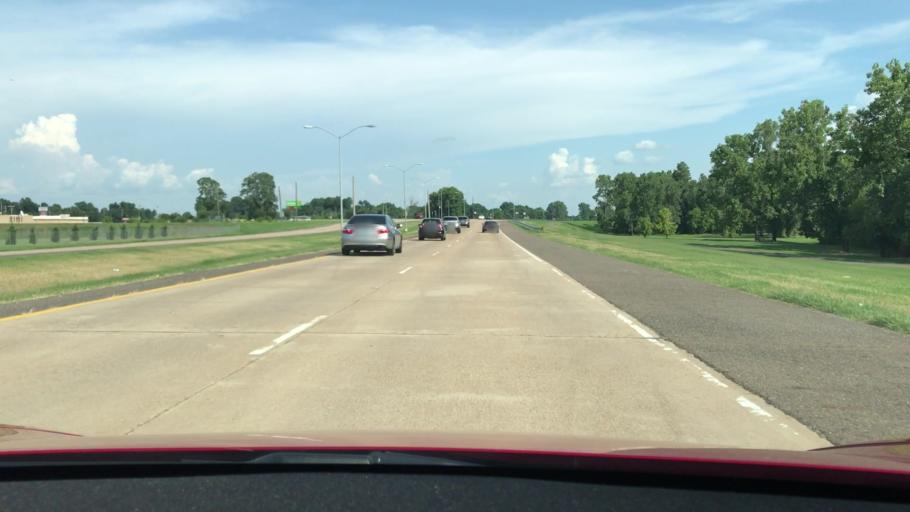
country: US
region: Louisiana
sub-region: Bossier Parish
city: Bossier City
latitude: 32.4805
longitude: -93.6822
